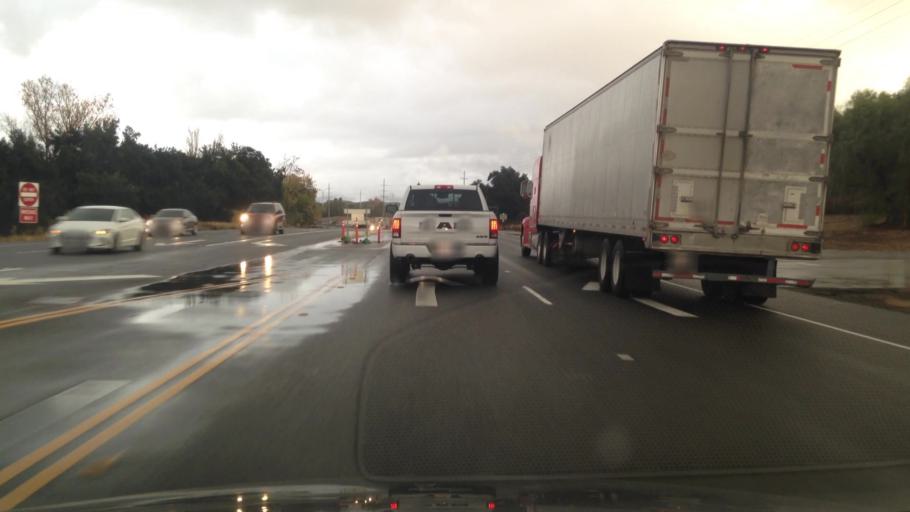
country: US
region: California
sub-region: Riverside County
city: Beaumont
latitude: 33.9341
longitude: -117.0337
